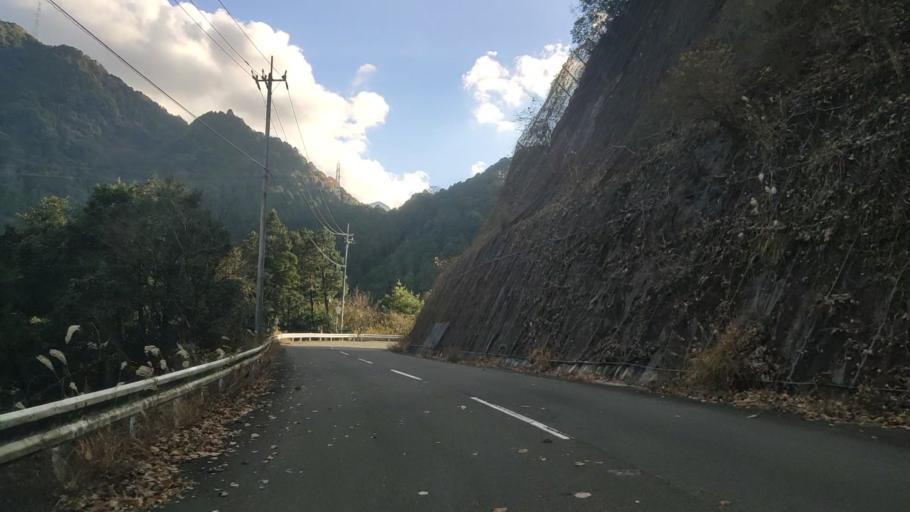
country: JP
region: Ehime
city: Saijo
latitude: 33.8681
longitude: 133.1622
